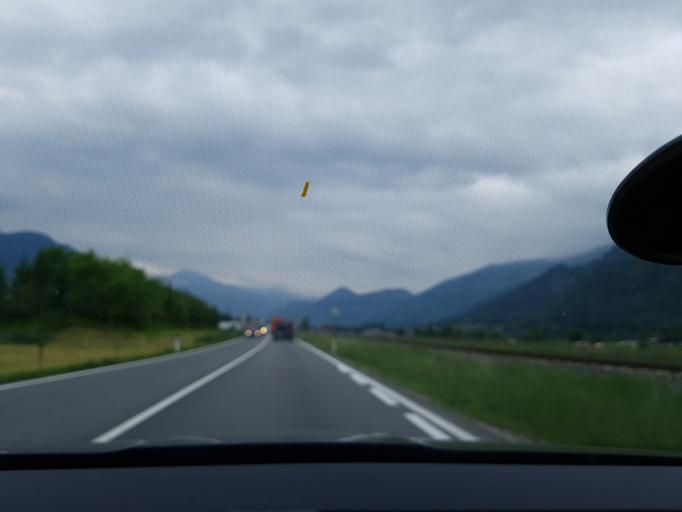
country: AT
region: Tyrol
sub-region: Politischer Bezirk Schwaz
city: Uderns
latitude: 47.3140
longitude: 11.8664
